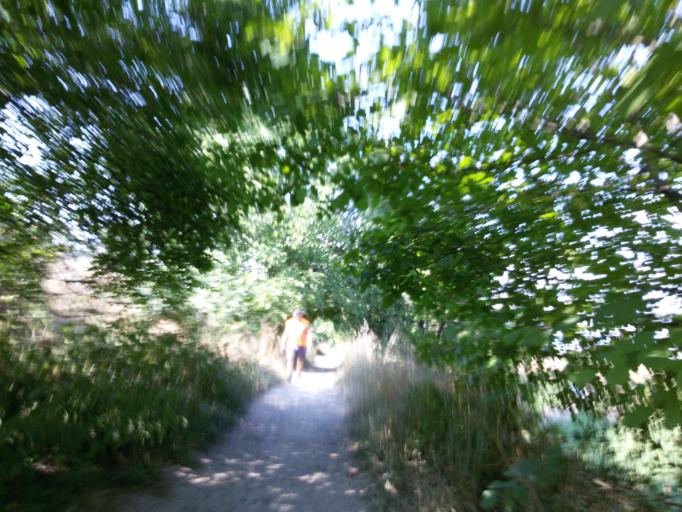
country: CZ
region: South Moravian
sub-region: Mesto Brno
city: Mokra Hora
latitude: 49.2490
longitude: 16.5903
